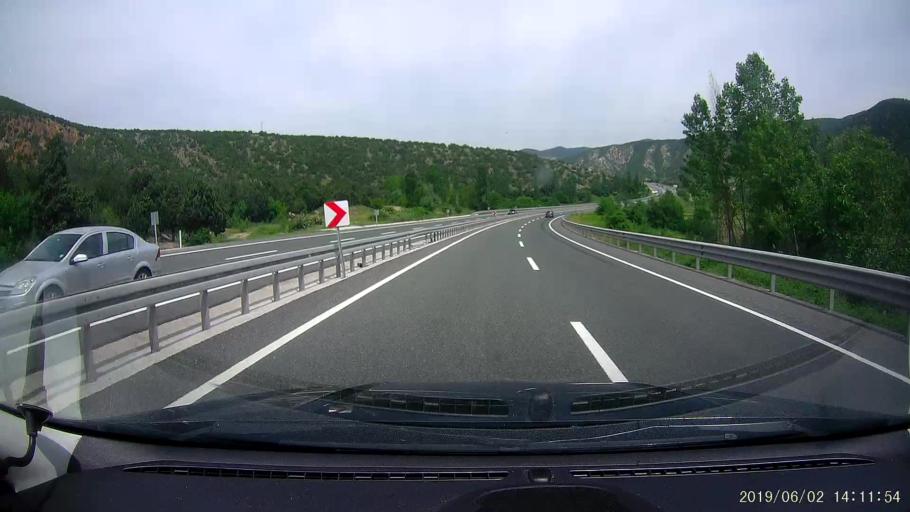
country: TR
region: Cankiri
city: Yaprakli
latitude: 40.9119
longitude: 33.7963
